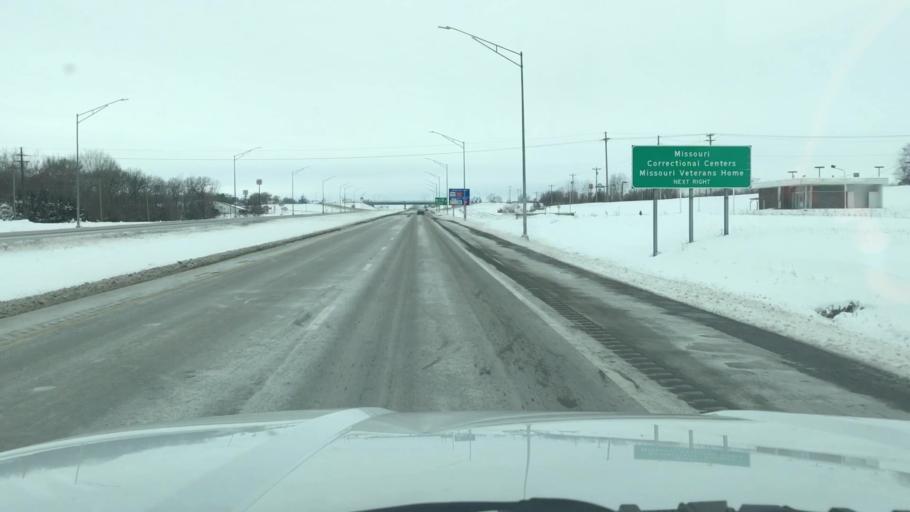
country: US
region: Missouri
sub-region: Clinton County
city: Cameron
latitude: 39.7540
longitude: -94.2232
